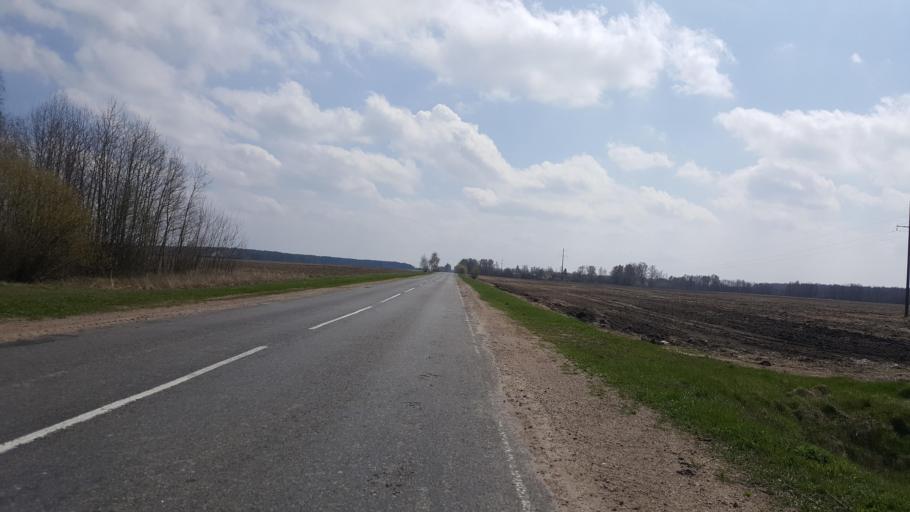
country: BY
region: Brest
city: Zhabinka
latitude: 52.2624
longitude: 23.9612
